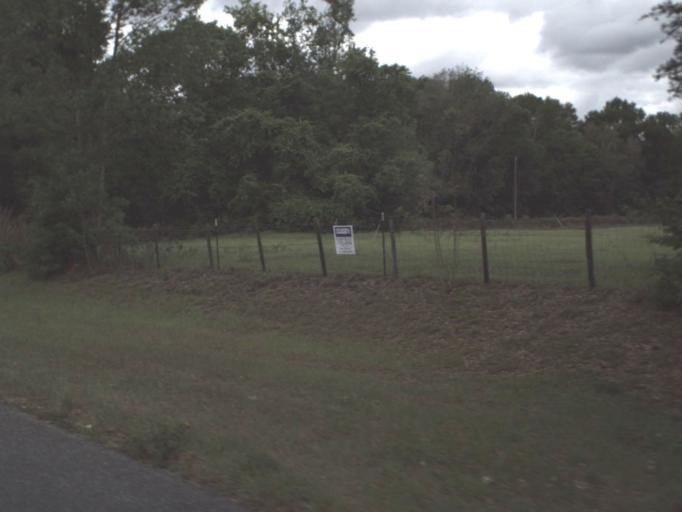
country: US
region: Florida
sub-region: Marion County
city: Ocala
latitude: 29.2593
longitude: -82.0900
